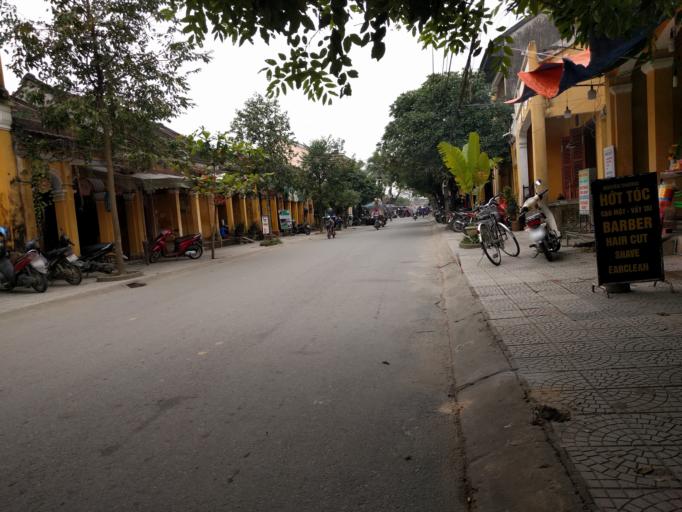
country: VN
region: Quang Nam
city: Hoi An
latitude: 15.8769
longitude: 108.3337
